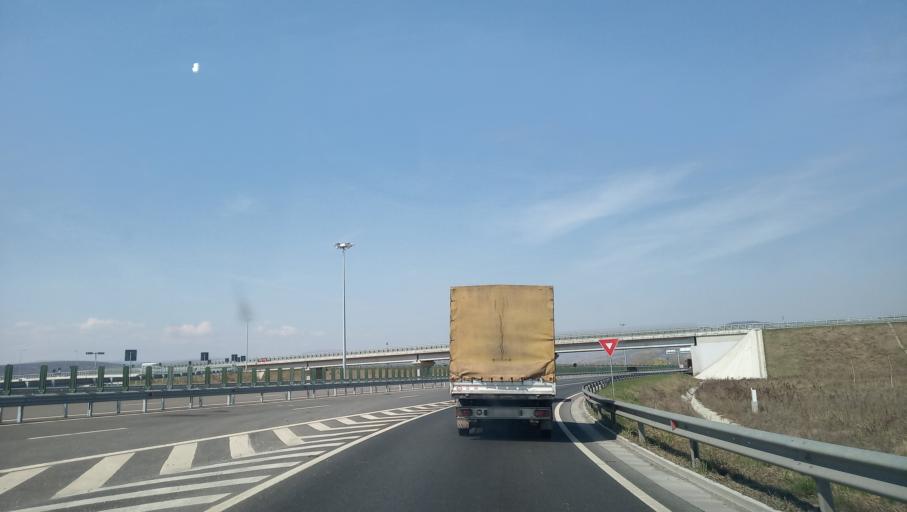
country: RO
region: Alba
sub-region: Municipiul Aiud
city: Aiud
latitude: 46.3279
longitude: 23.7299
